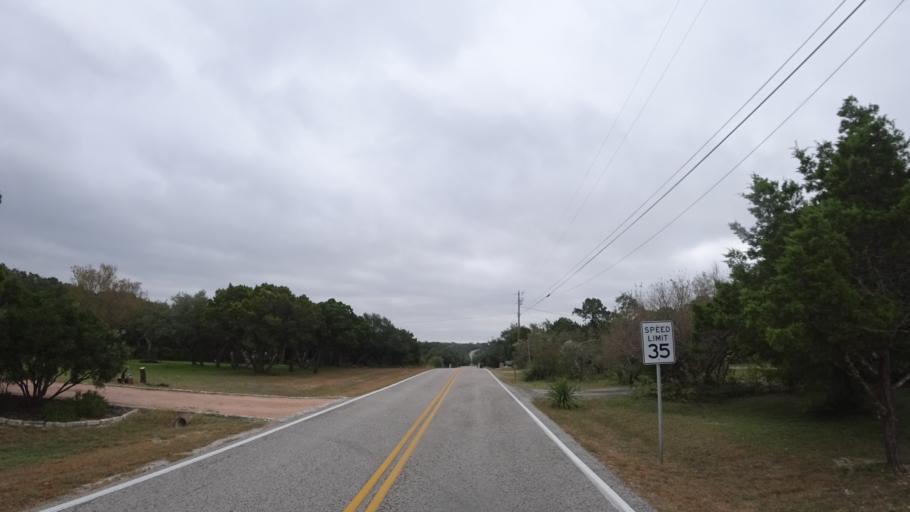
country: US
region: Texas
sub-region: Travis County
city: Bee Cave
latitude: 30.2634
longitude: -97.9187
